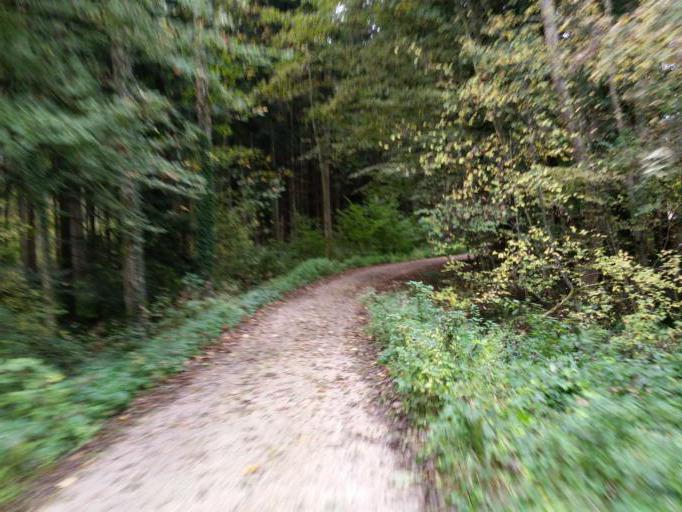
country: CH
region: Thurgau
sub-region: Arbon District
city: Uttwil
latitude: 47.5661
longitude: 9.3359
